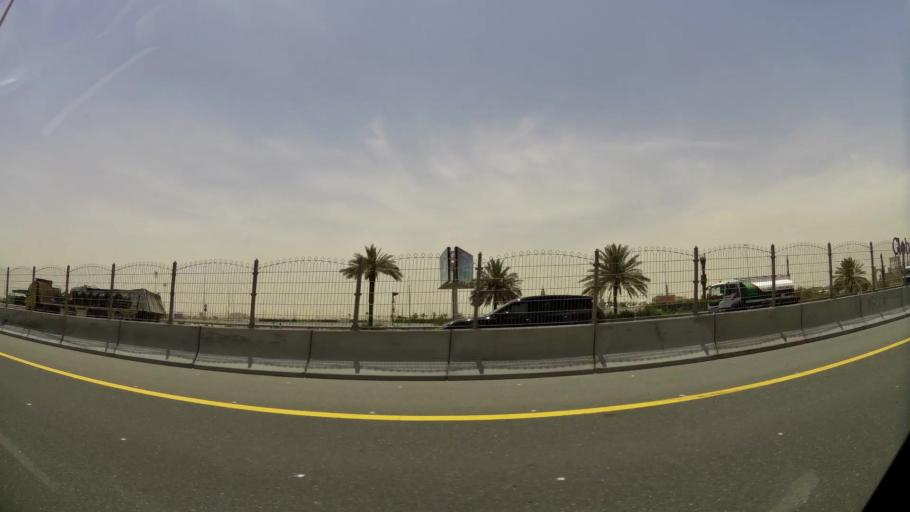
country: AE
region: Dubai
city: Dubai
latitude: 25.0750
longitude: 55.3056
